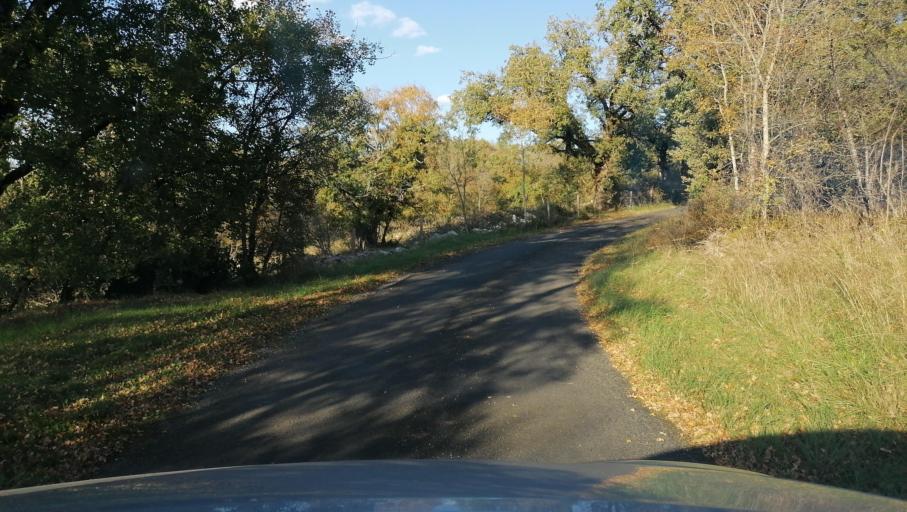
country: FR
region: Midi-Pyrenees
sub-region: Departement du Lot
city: Vayrac
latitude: 44.8932
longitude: 1.6583
